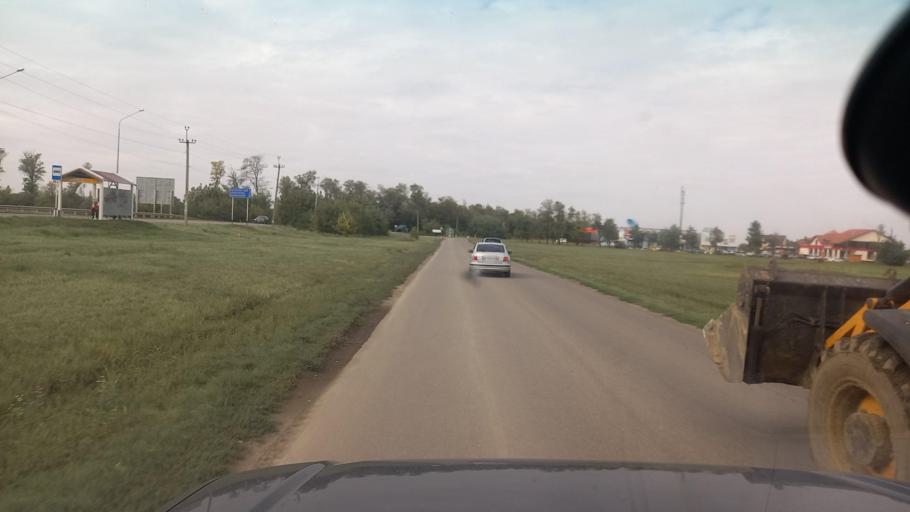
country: RU
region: Krasnodarskiy
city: Krasnodar
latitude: 45.1149
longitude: 38.9209
